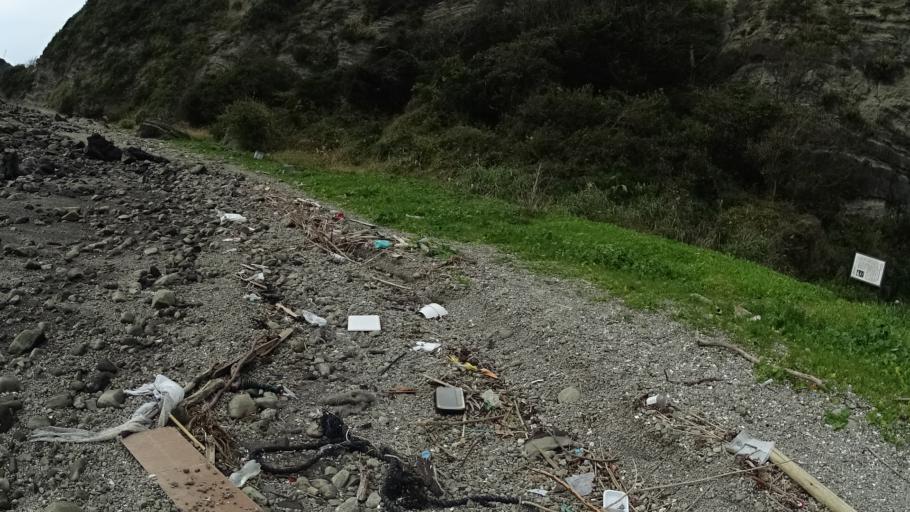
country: JP
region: Kanagawa
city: Miura
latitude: 35.1397
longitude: 139.6548
